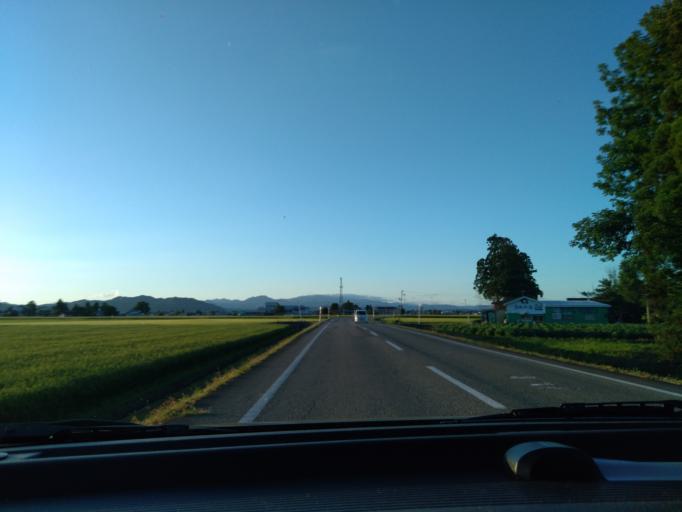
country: JP
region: Akita
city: Omagari
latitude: 39.4918
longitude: 140.5594
